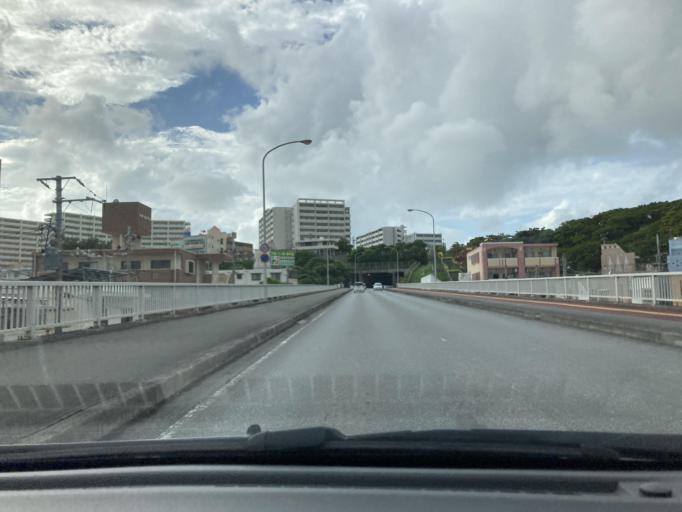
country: JP
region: Okinawa
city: Tomigusuku
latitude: 26.1843
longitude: 127.6755
